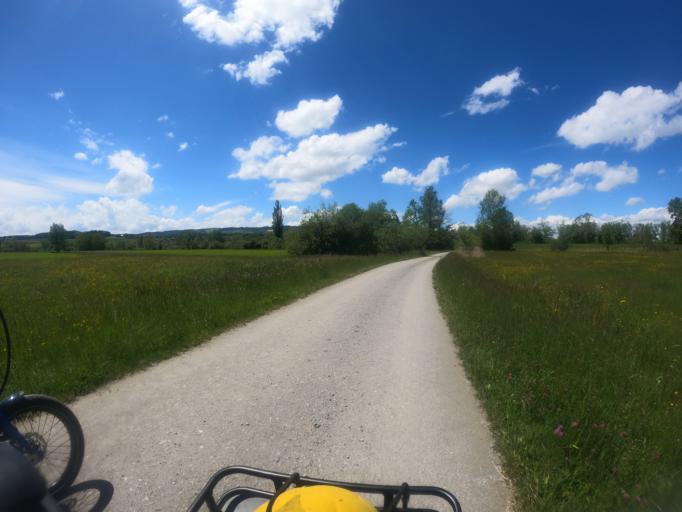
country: CH
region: Zurich
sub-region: Bezirk Affoltern
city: Obfelden / Oberlunnern
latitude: 47.2345
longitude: 8.4070
